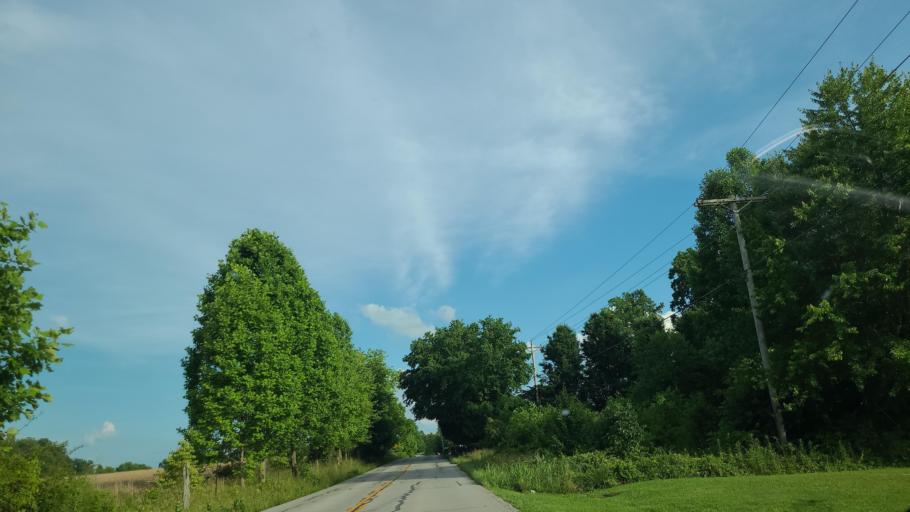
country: US
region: Kentucky
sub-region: Whitley County
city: Corbin
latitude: 36.9014
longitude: -84.2360
